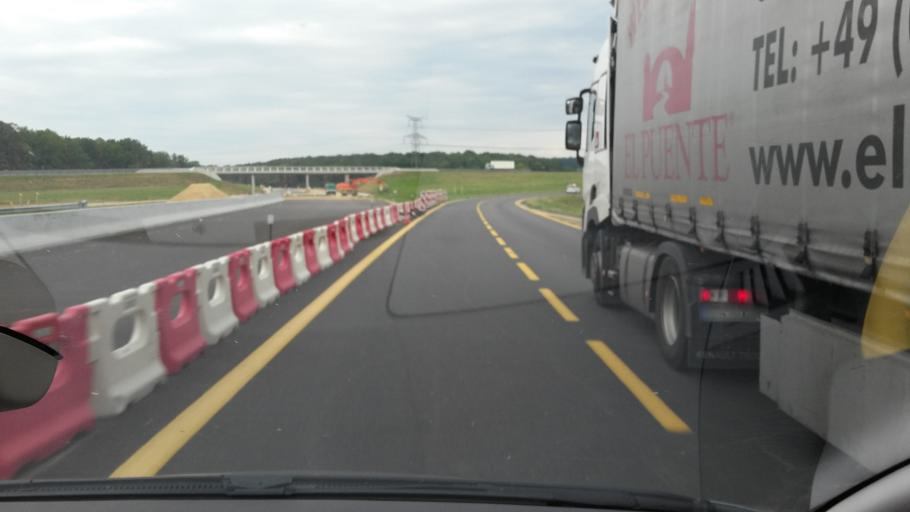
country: FR
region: Champagne-Ardenne
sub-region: Departement des Ardennes
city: La Francheville
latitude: 49.7171
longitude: 4.7004
